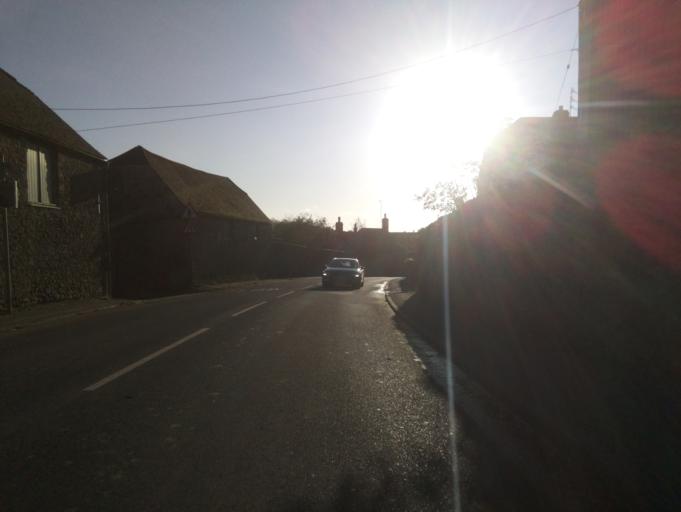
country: GB
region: England
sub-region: Dorset
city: Sherborne
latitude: 50.9518
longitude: -2.5041
